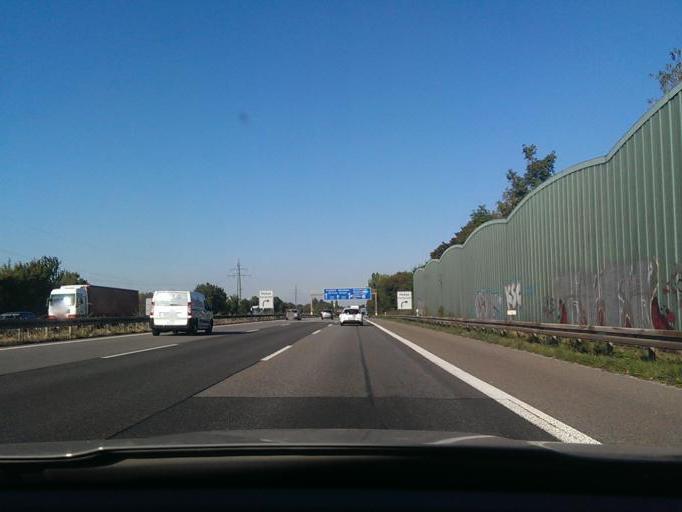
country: DE
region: Baden-Wuerttemberg
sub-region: Karlsruhe Region
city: Ettlingen
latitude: 48.9490
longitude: 8.3725
